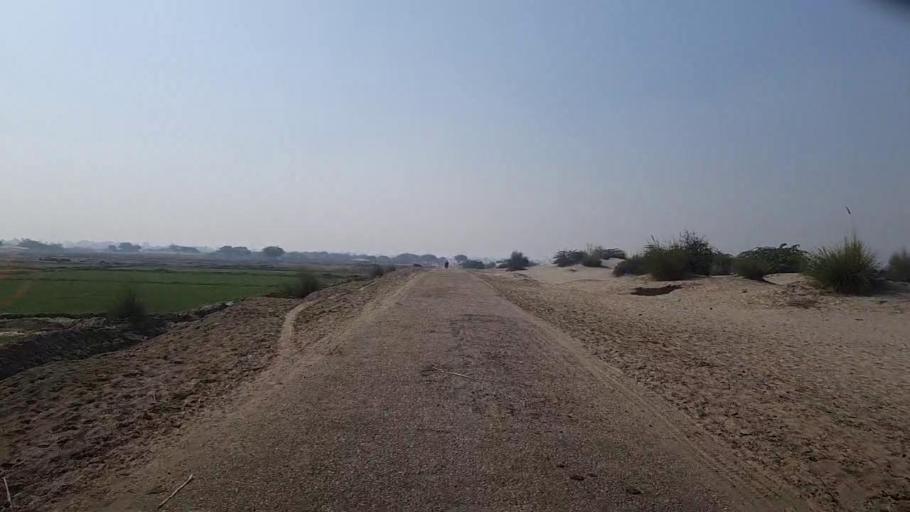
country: PK
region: Sindh
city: Bozdar
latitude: 27.2583
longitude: 68.6170
